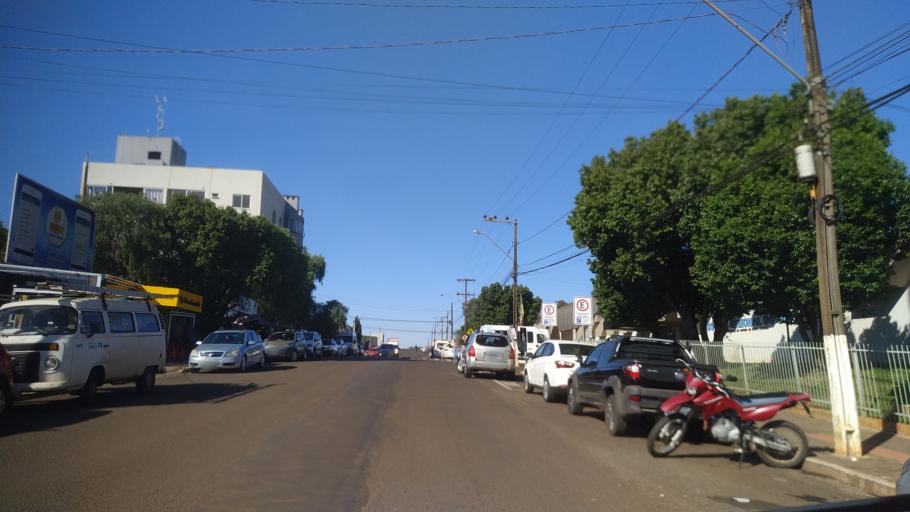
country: BR
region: Santa Catarina
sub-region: Chapeco
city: Chapeco
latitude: -27.1075
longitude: -52.5977
